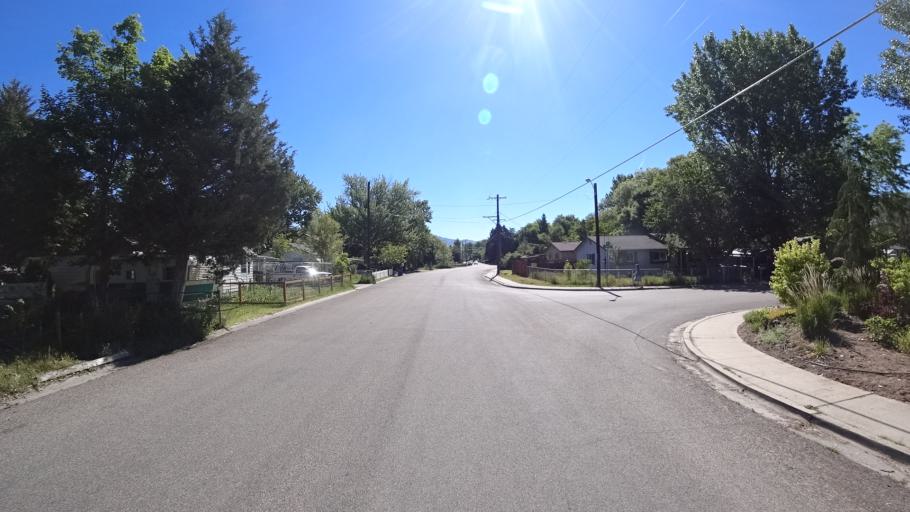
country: US
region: Idaho
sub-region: Ada County
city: Garden City
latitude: 43.6483
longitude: -116.2371
